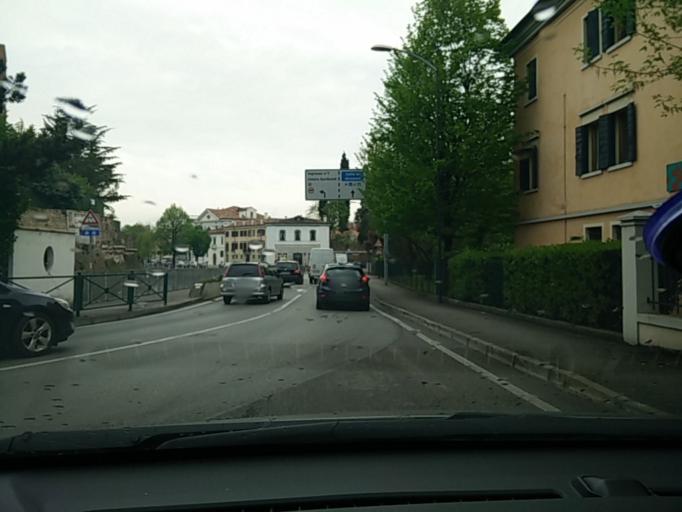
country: IT
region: Veneto
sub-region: Provincia di Treviso
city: Treviso
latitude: 45.6624
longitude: 12.2527
